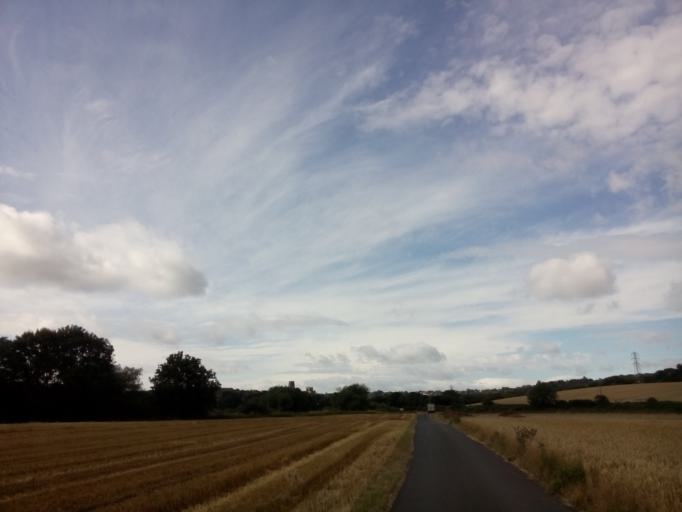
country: GB
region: England
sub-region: County Durham
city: Durham
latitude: 54.7890
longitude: -1.5625
